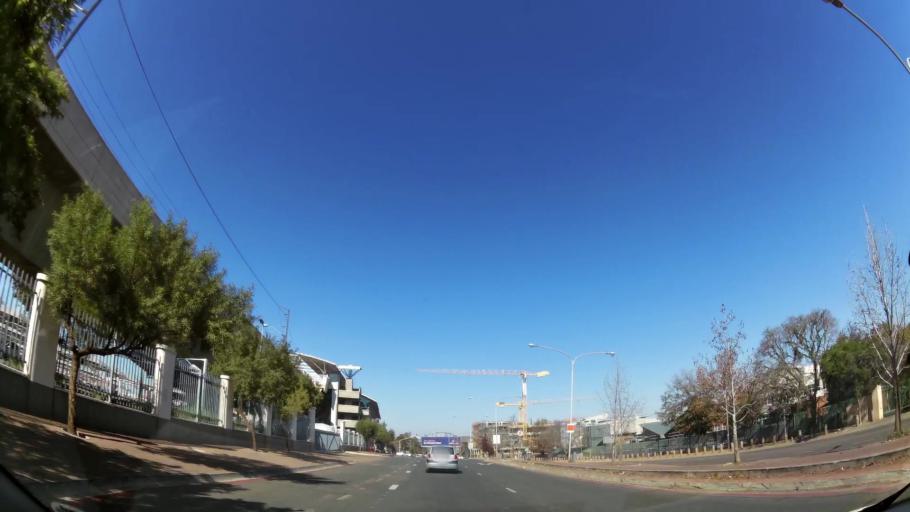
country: ZA
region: Gauteng
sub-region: City of Tshwane Metropolitan Municipality
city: Centurion
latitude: -25.8509
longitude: 28.1886
